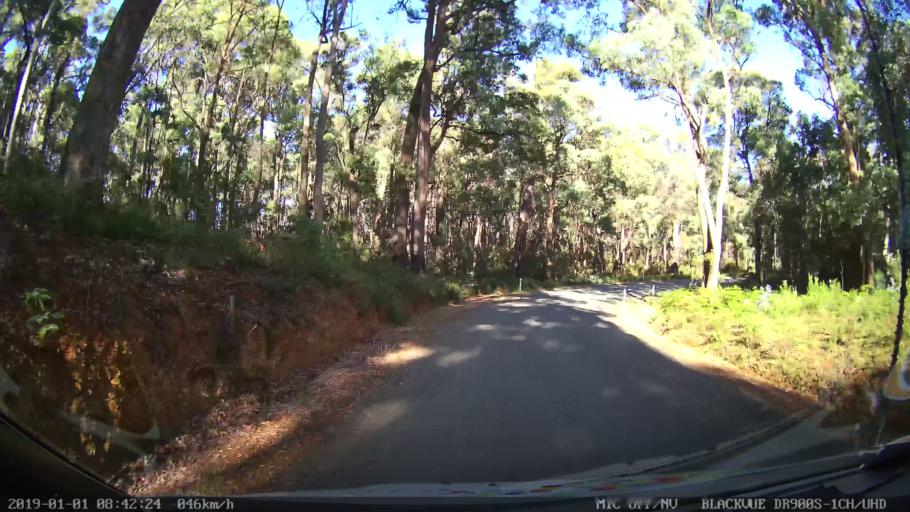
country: AU
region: New South Wales
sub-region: Snowy River
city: Jindabyne
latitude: -36.3236
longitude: 148.1938
